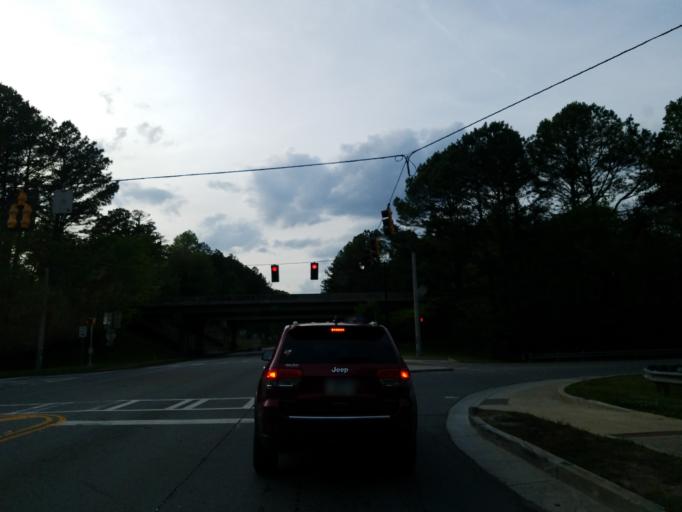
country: US
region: Georgia
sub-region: Cherokee County
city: Canton
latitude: 34.2231
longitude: -84.4836
